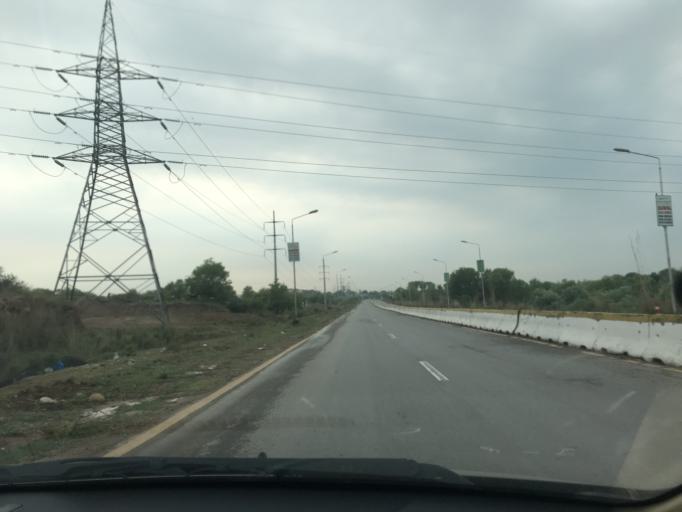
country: PK
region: Islamabad
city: Islamabad
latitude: 33.6983
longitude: 73.1820
